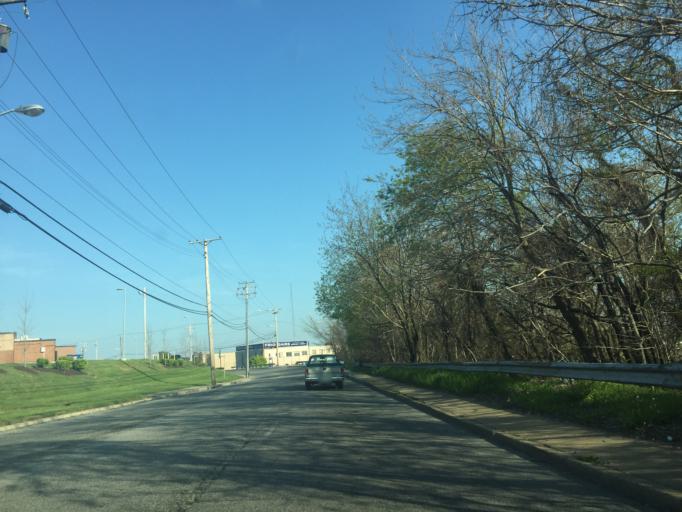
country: US
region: Maryland
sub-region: City of Baltimore
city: Baltimore
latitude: 39.3141
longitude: -76.5717
